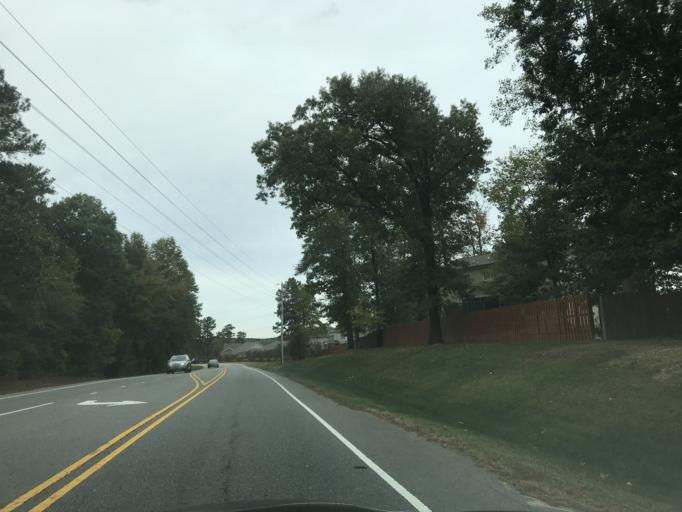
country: US
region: North Carolina
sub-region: Wake County
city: Rolesville
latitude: 35.9097
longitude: -78.5046
